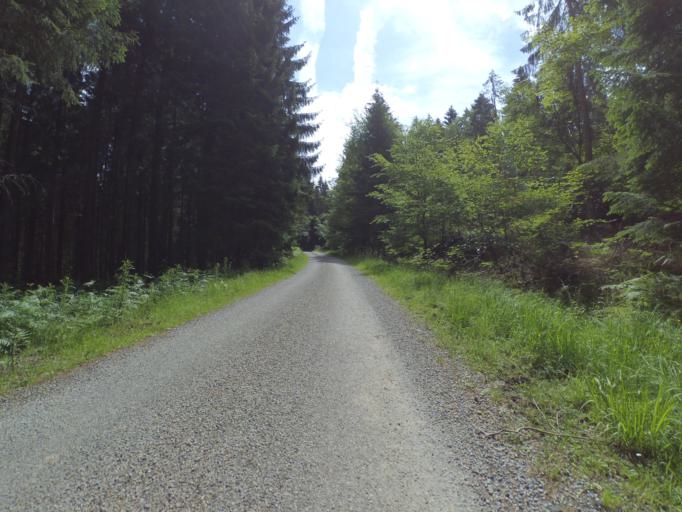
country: BE
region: Wallonia
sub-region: Province de Liege
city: Raeren
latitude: 50.6004
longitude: 6.1205
